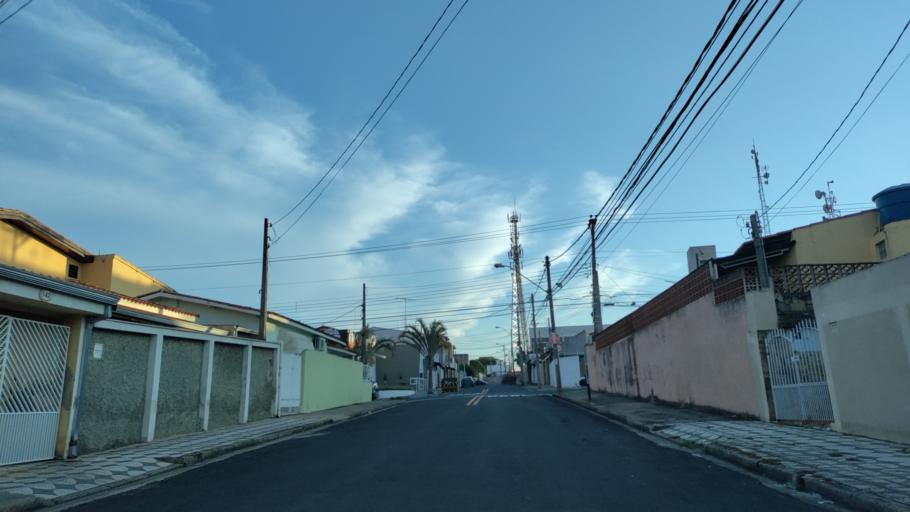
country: BR
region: Sao Paulo
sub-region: Sorocaba
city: Sorocaba
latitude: -23.4845
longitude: -47.4509
